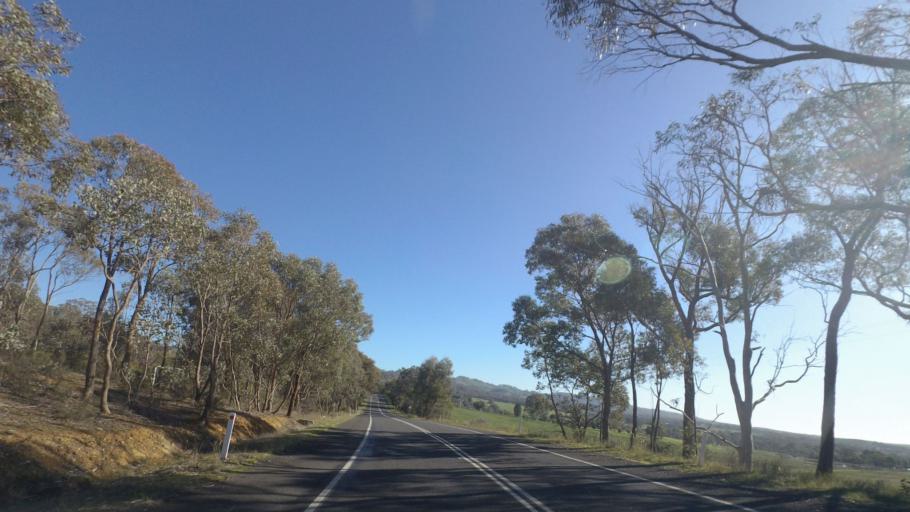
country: AU
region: Victoria
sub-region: Greater Bendigo
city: Kennington
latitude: -36.9106
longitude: 144.3249
